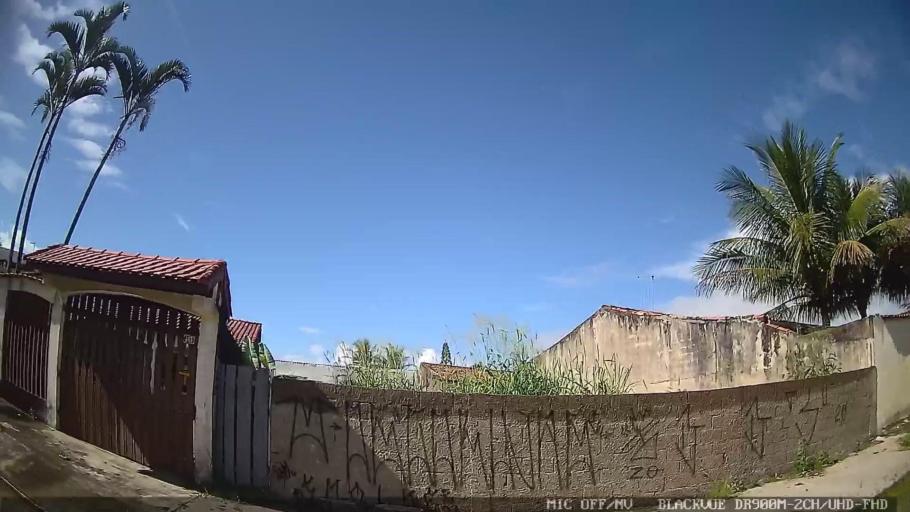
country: BR
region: Sao Paulo
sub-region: Itanhaem
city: Itanhaem
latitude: -24.2406
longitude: -46.8846
